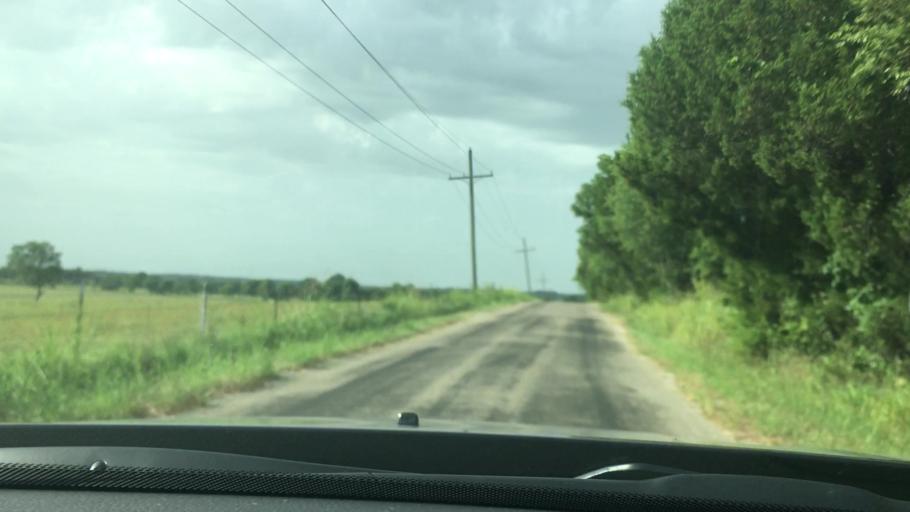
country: US
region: Oklahoma
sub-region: Pontotoc County
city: Byng
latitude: 34.8734
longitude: -96.5785
